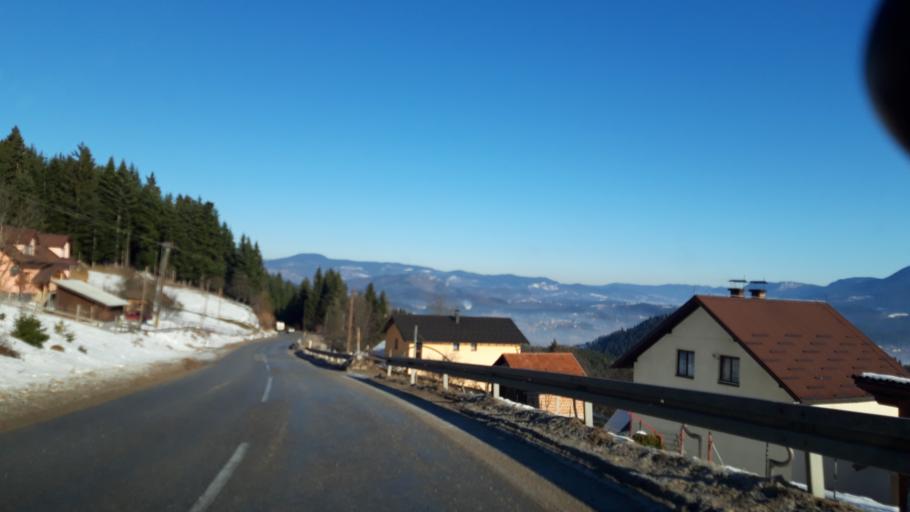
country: BA
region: Republika Srpska
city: Koran
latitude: 43.7927
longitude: 18.5559
